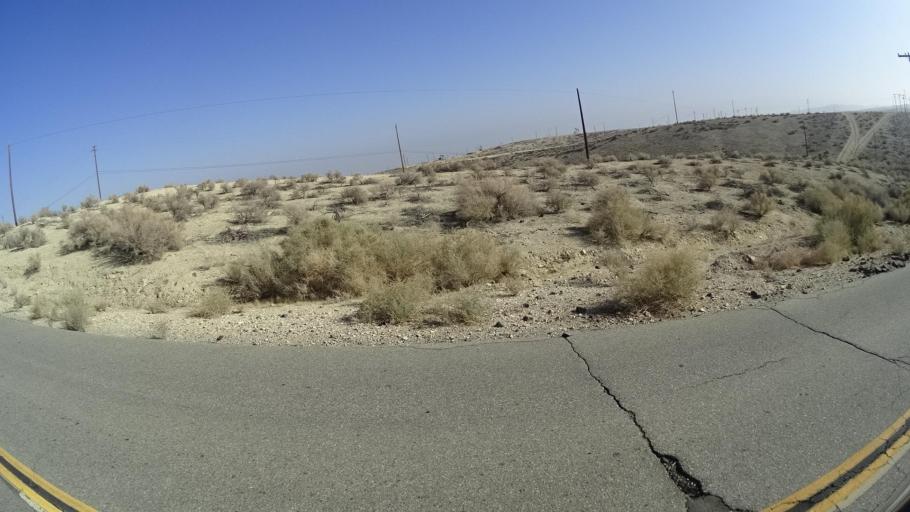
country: US
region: California
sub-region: Kern County
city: Taft Heights
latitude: 35.1467
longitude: -119.5142
